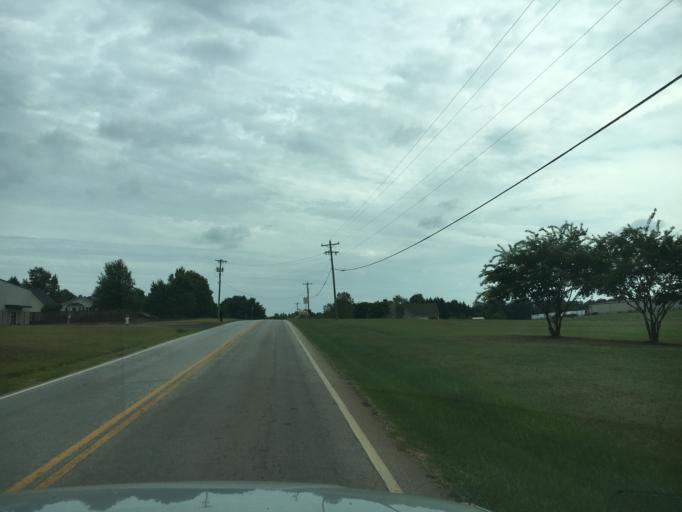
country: US
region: South Carolina
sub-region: Spartanburg County
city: Duncan
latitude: 34.9103
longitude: -82.1637
